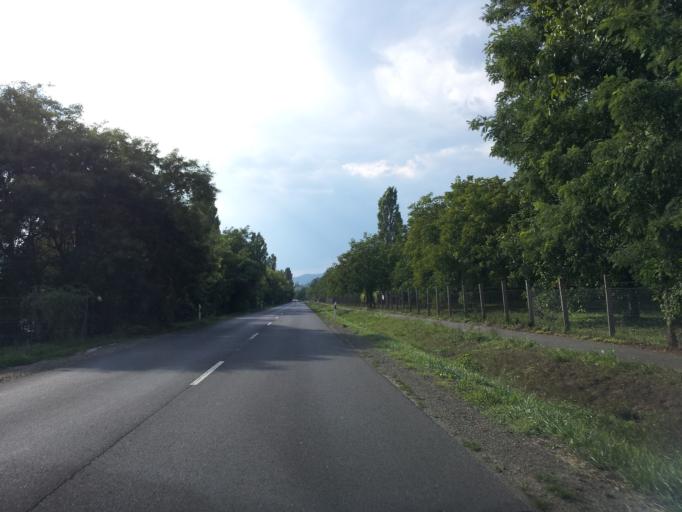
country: HU
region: Pest
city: Veroce
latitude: 47.8186
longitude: 19.0516
